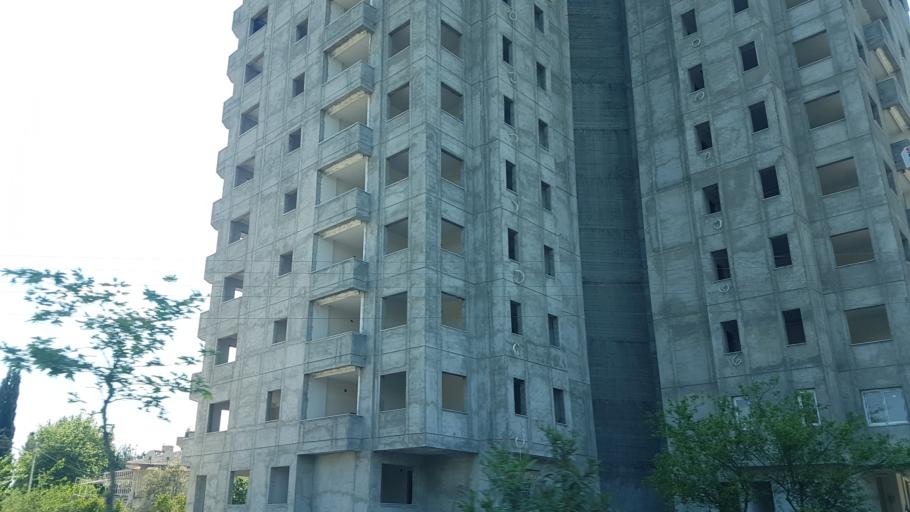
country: TR
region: Adana
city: Adana
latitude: 37.0214
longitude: 35.3712
